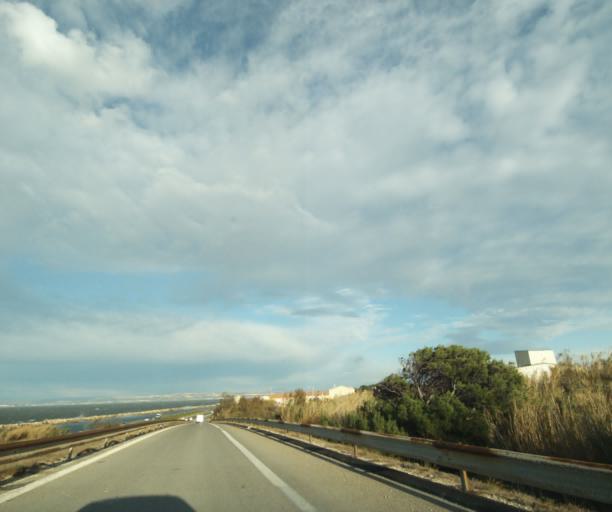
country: FR
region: Provence-Alpes-Cote d'Azur
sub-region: Departement des Bouches-du-Rhone
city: Martigues
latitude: 43.4010
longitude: 5.1044
